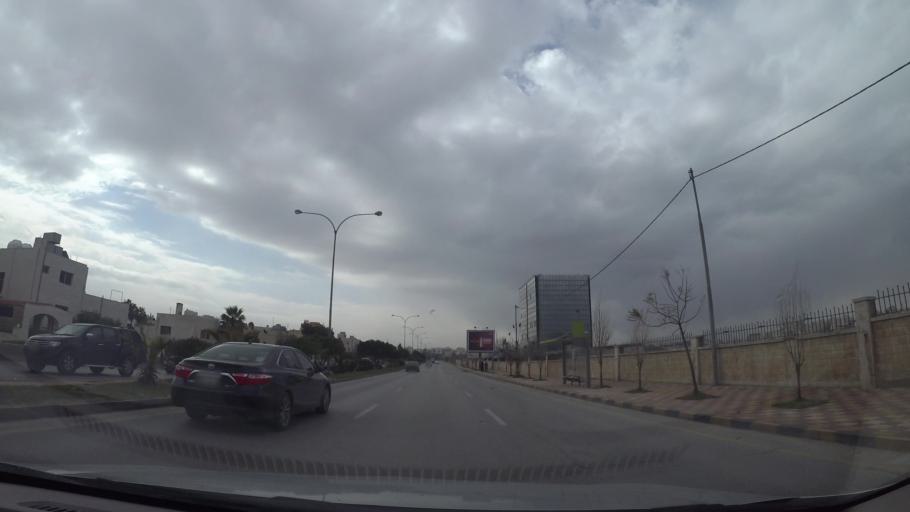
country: JO
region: Amman
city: Umm as Summaq
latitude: 31.9004
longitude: 35.8523
